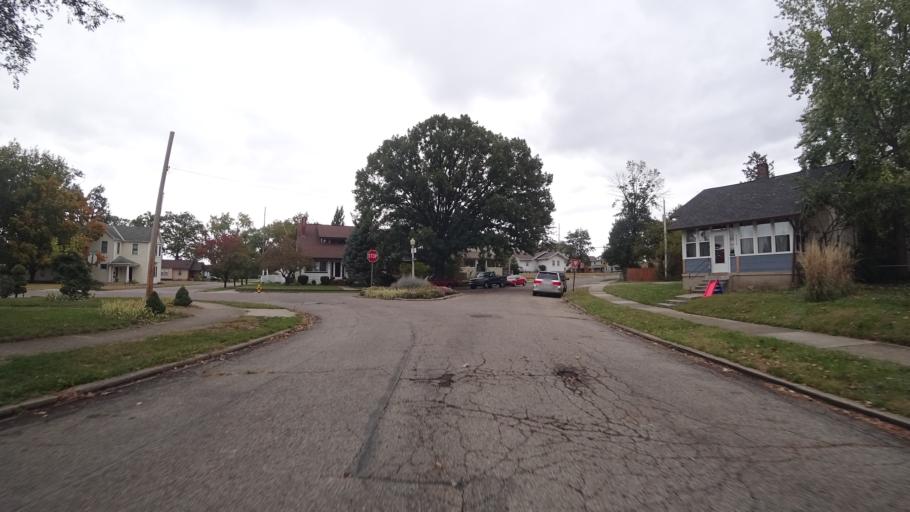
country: US
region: Ohio
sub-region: Butler County
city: Fairfield
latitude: 39.3668
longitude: -84.5589
